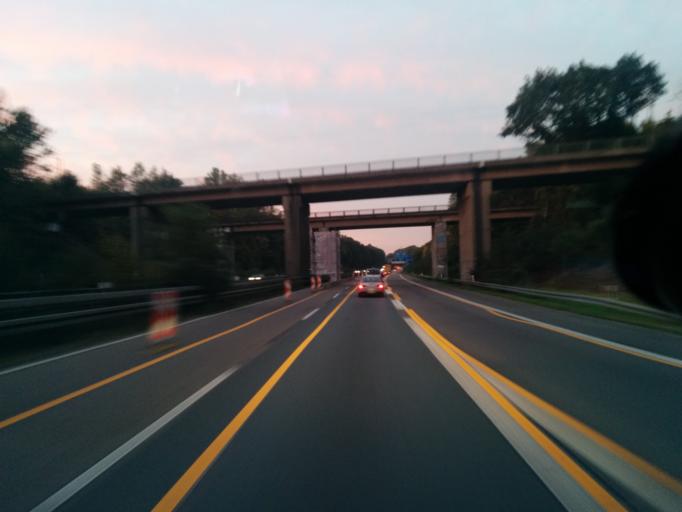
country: DE
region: North Rhine-Westphalia
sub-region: Regierungsbezirk Arnsberg
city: Bochum
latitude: 51.4806
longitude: 7.2789
